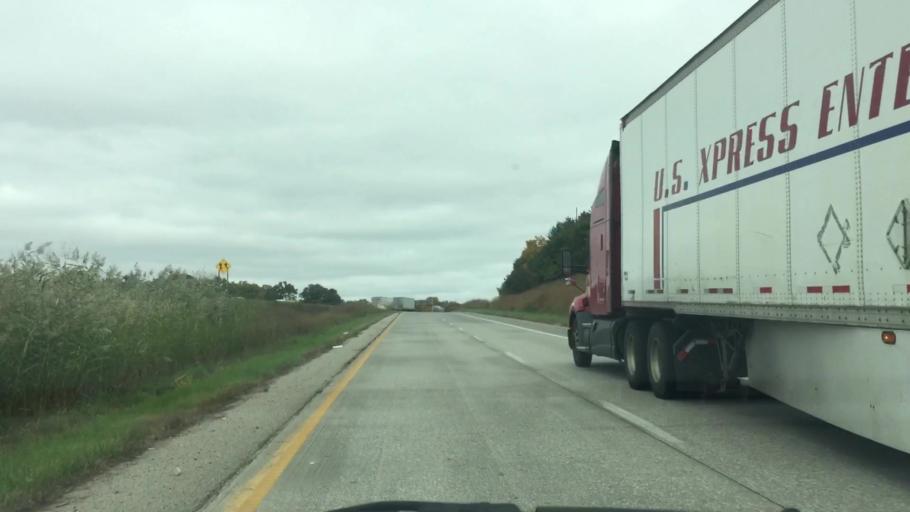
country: US
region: Iowa
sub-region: Polk County
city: Clive
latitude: 41.6163
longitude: -93.7761
